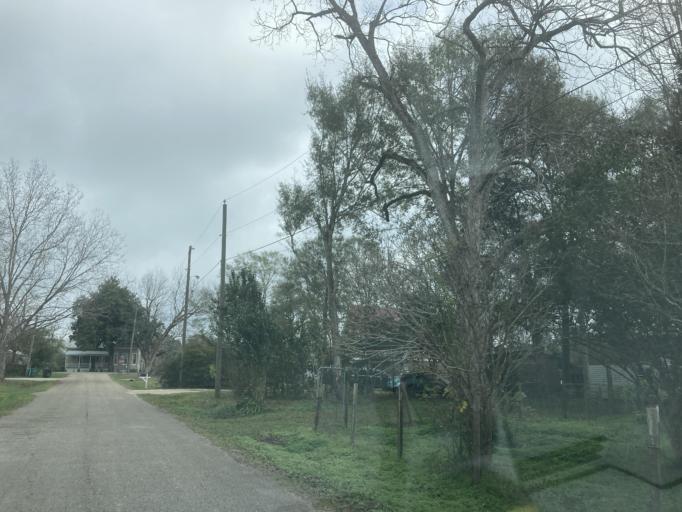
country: US
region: Mississippi
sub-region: Stone County
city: Wiggins
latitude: 30.8941
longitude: -89.1625
